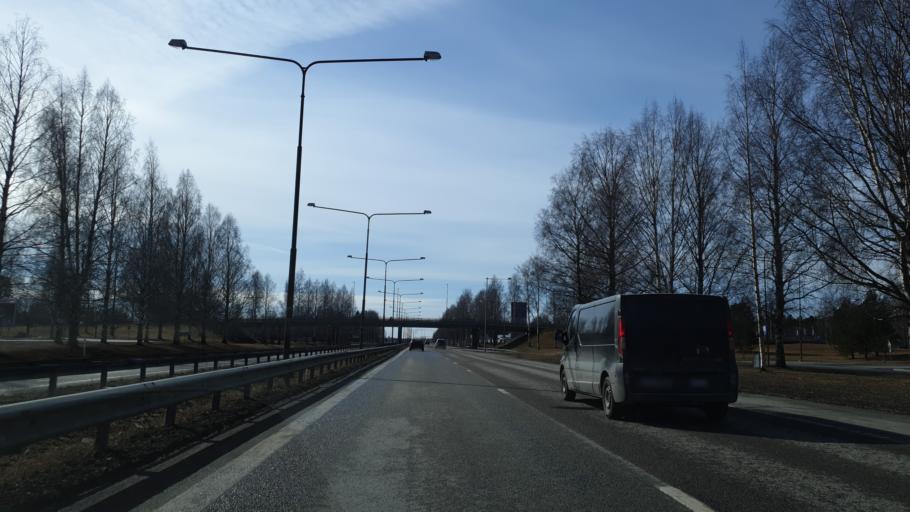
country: SE
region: Vaesterbotten
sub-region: Umea Kommun
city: Umea
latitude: 63.8171
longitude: 20.2499
